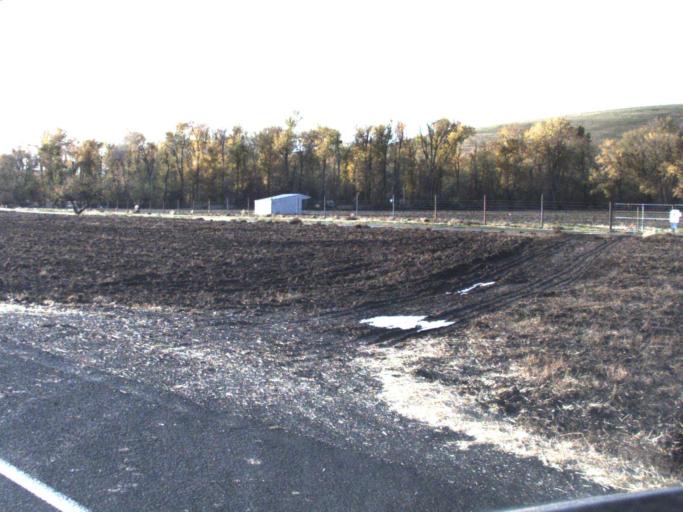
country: US
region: Washington
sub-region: Columbia County
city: Dayton
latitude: 46.2887
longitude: -118.0348
